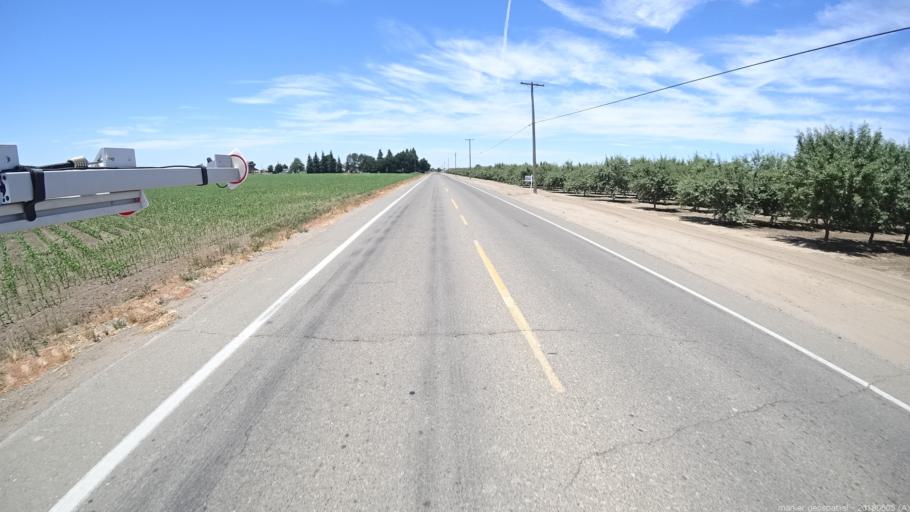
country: US
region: California
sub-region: Madera County
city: Chowchilla
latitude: 37.1127
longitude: -120.3117
